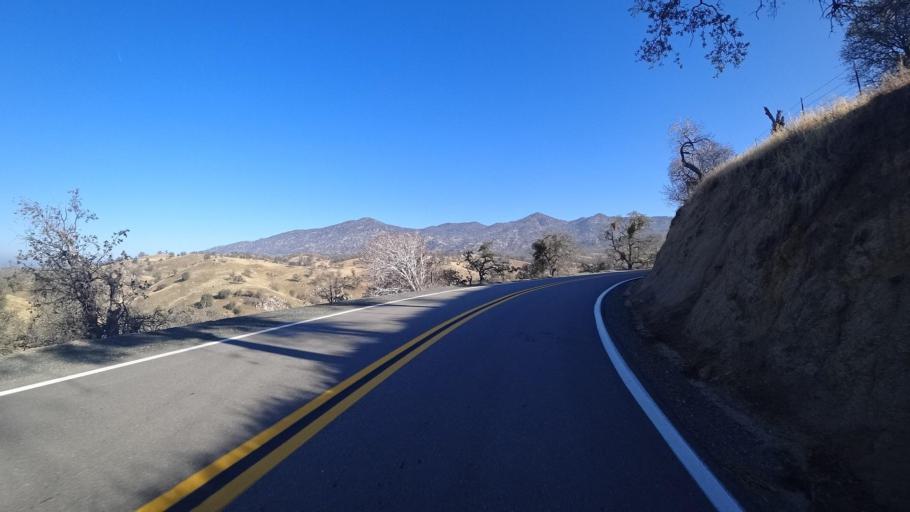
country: US
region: California
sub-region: Kern County
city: Alta Sierra
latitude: 35.7208
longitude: -118.8019
